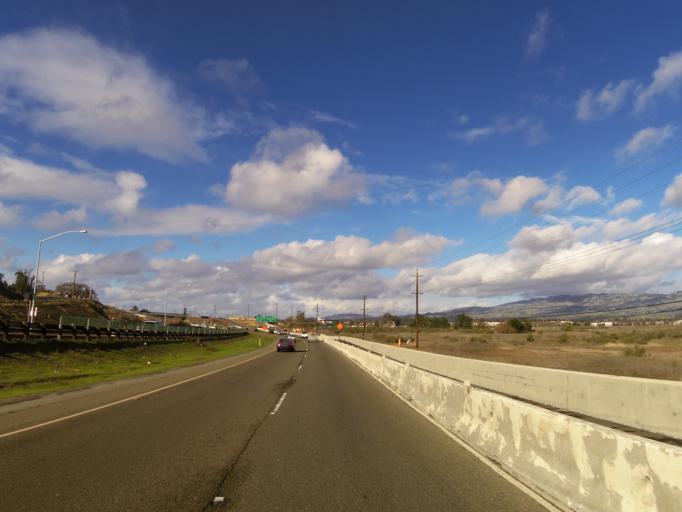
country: US
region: California
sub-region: Sonoma County
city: Petaluma
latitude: 38.2161
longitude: -122.6031
